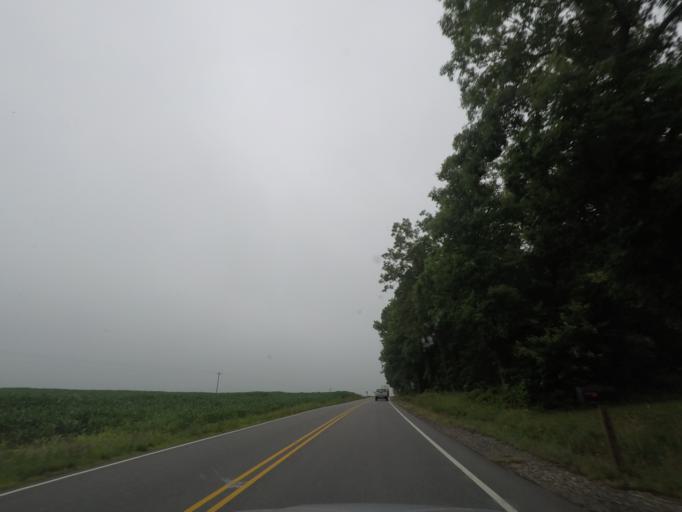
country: US
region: Virginia
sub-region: Prince Edward County
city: Farmville
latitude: 37.3581
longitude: -78.4827
